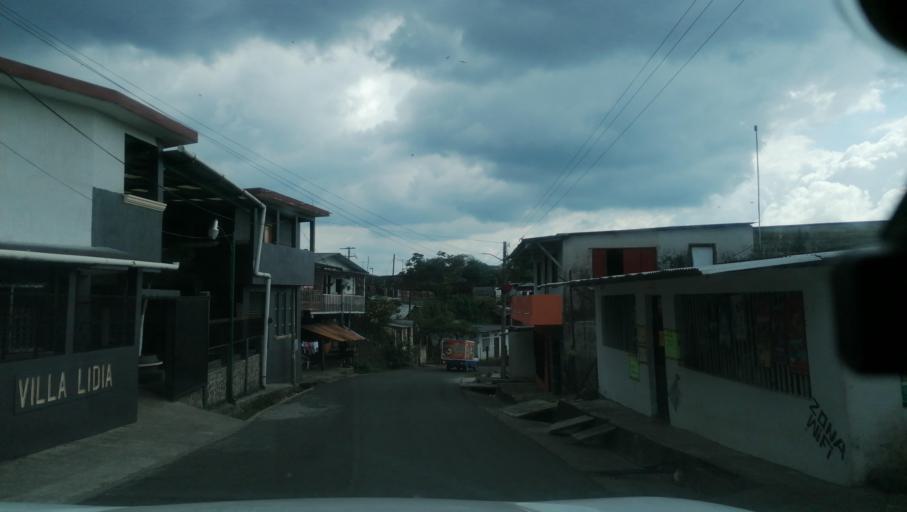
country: MX
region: Chiapas
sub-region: Cacahoatan
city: Benito Juarez
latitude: 15.0751
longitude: -92.1986
